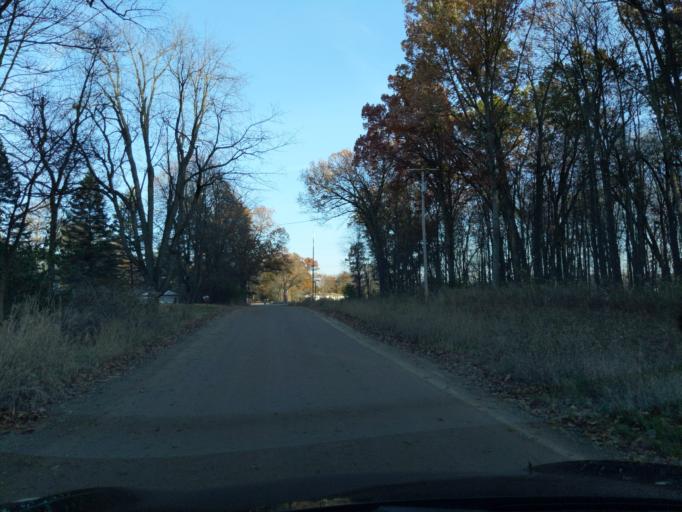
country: US
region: Michigan
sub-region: Clinton County
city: Bath
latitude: 42.7986
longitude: -84.4857
